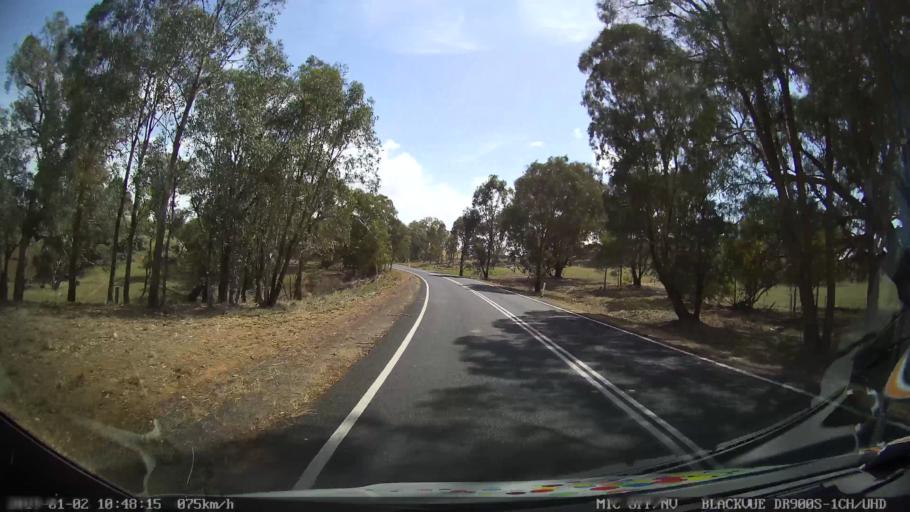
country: AU
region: New South Wales
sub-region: Cootamundra
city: Cootamundra
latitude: -34.7385
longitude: 148.2769
